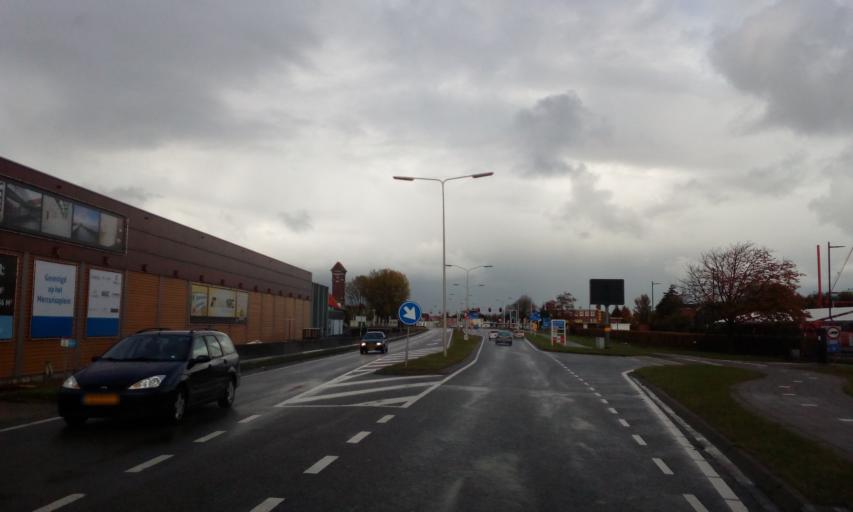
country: NL
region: South Holland
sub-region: Gemeente Westland
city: Poeldijk
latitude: 52.0203
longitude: 4.2130
